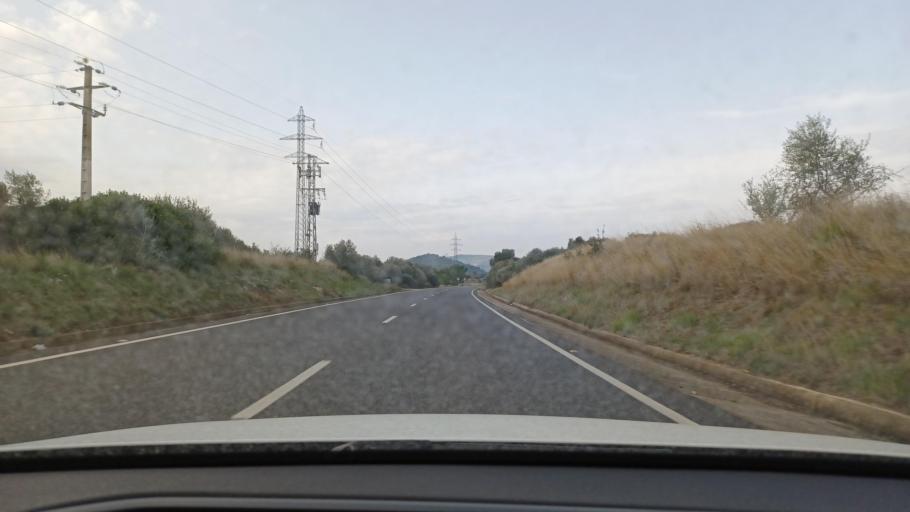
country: ES
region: Catalonia
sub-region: Provincia de Tarragona
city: Masdenverge
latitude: 40.6973
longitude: 0.5419
